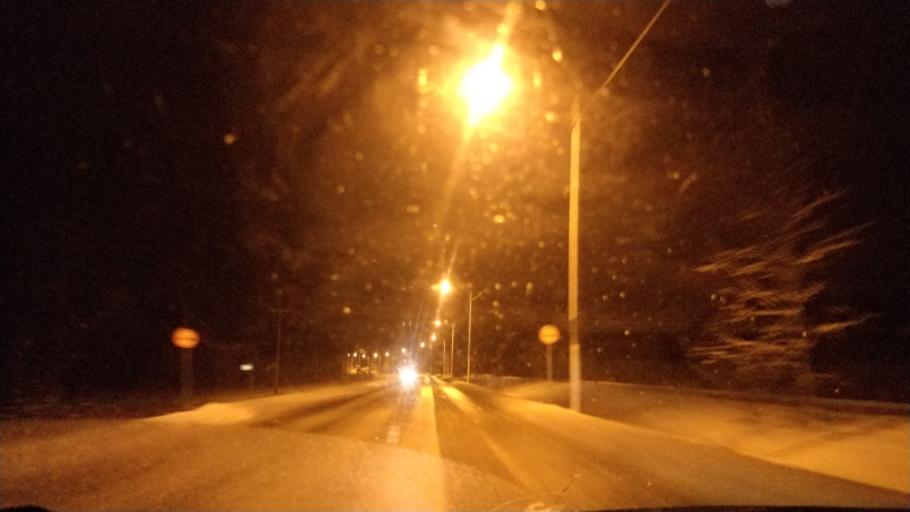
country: FI
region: Lapland
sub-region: Rovaniemi
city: Rovaniemi
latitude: 66.3037
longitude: 25.3559
